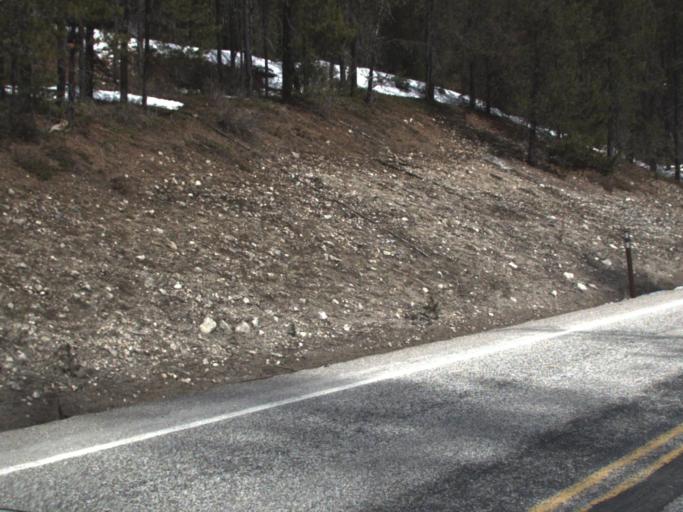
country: US
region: Washington
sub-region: Stevens County
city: Colville
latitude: 48.6469
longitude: -117.5146
